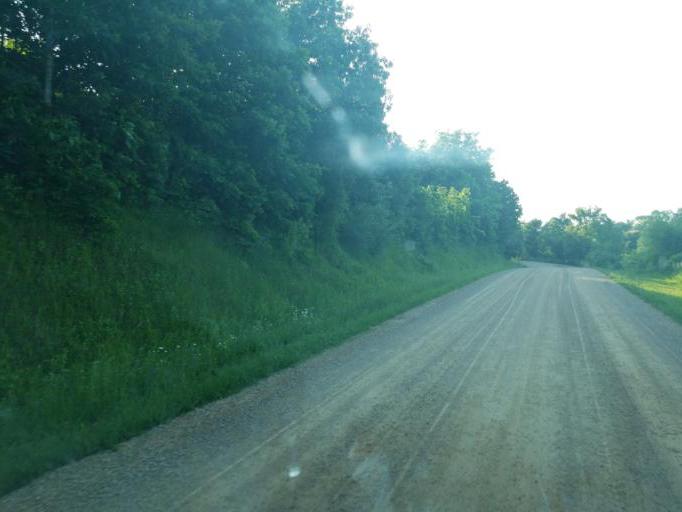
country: US
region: Wisconsin
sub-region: Vernon County
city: Hillsboro
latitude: 43.6288
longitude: -90.3409
